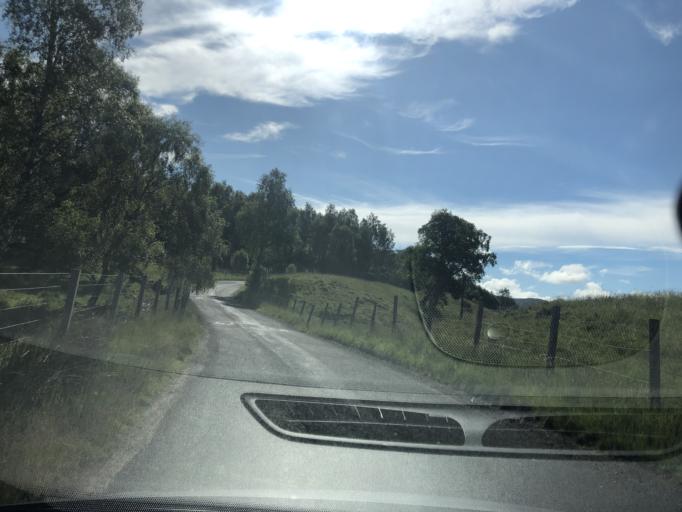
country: GB
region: Scotland
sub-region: Angus
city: Kirriemuir
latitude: 56.8388
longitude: -3.0894
